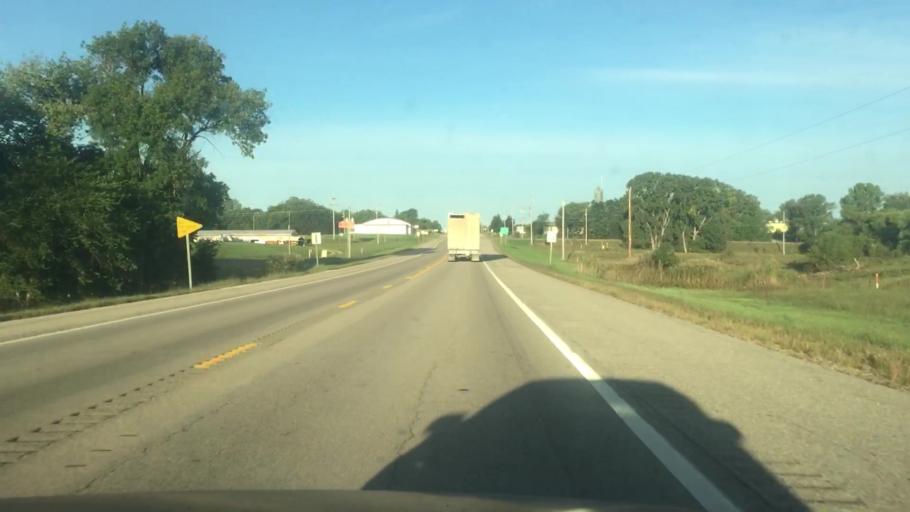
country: US
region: Kansas
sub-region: Marshall County
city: Marysville
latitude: 39.8424
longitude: -96.5974
